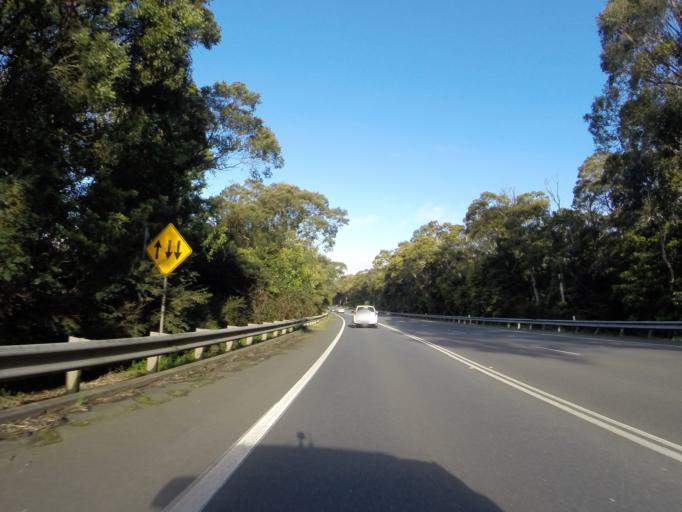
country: AU
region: New South Wales
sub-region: Shoalhaven Shire
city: Kangaroo Valley
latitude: -34.5886
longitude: 150.5622
